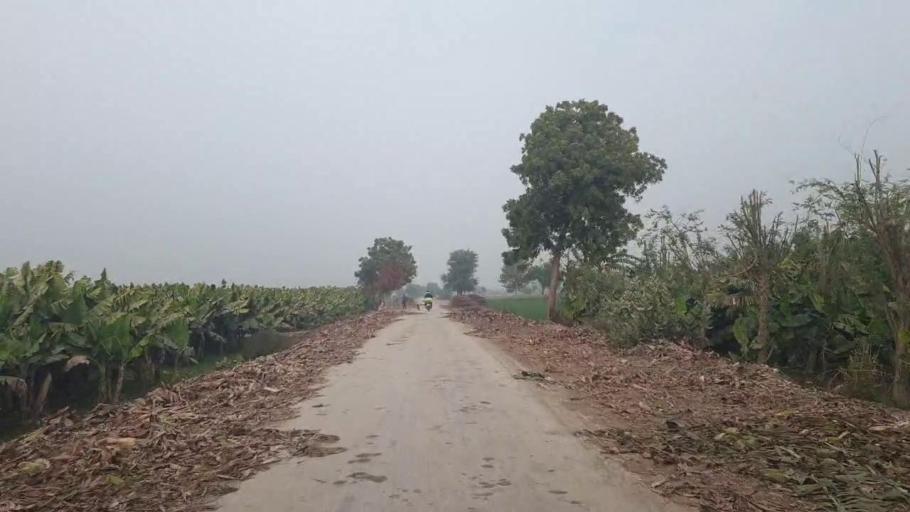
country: PK
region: Sindh
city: Tando Adam
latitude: 25.7637
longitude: 68.7026
